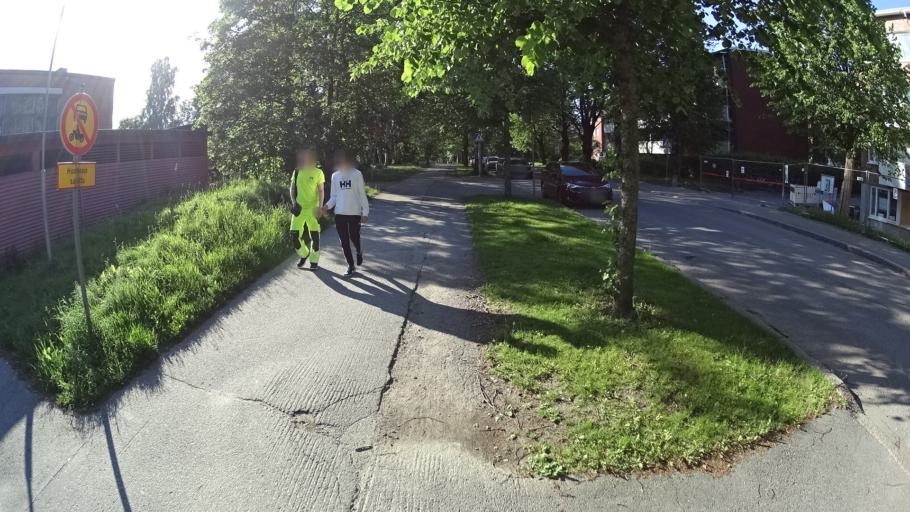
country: FI
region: Uusimaa
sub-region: Helsinki
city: Vantaa
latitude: 60.2142
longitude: 25.0998
